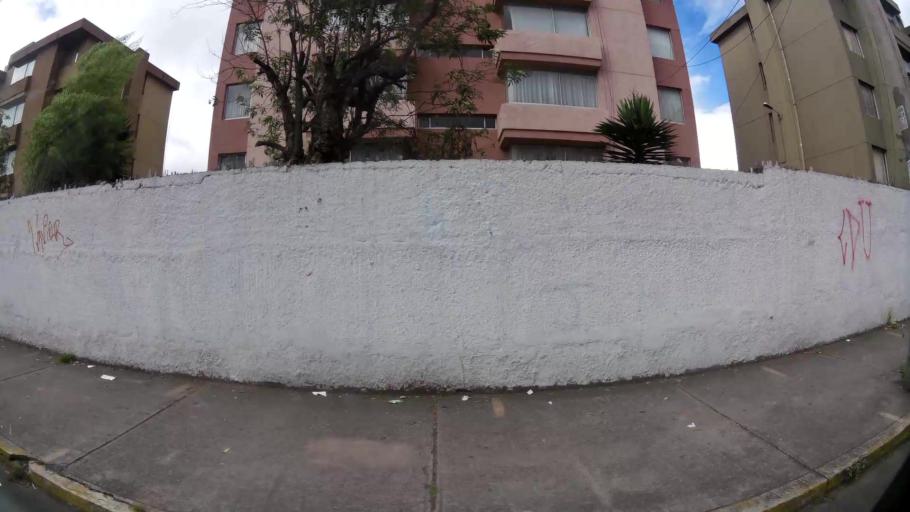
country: EC
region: Pichincha
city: Quito
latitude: -0.1332
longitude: -78.4977
